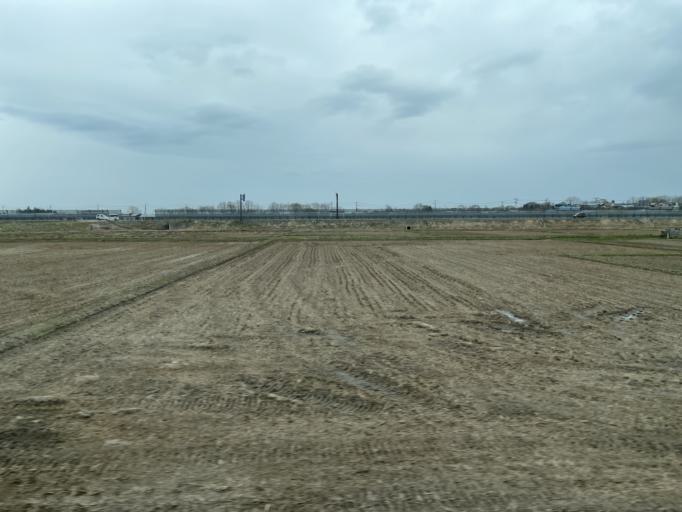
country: JP
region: Aomori
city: Namioka
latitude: 40.7011
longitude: 140.5721
